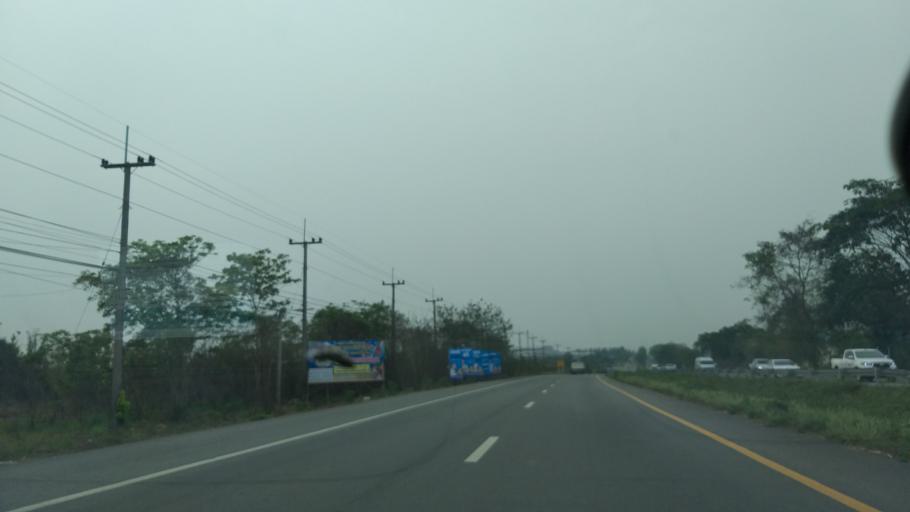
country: TH
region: Chachoengsao
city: Plaeng Yao
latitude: 13.4955
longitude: 101.2729
